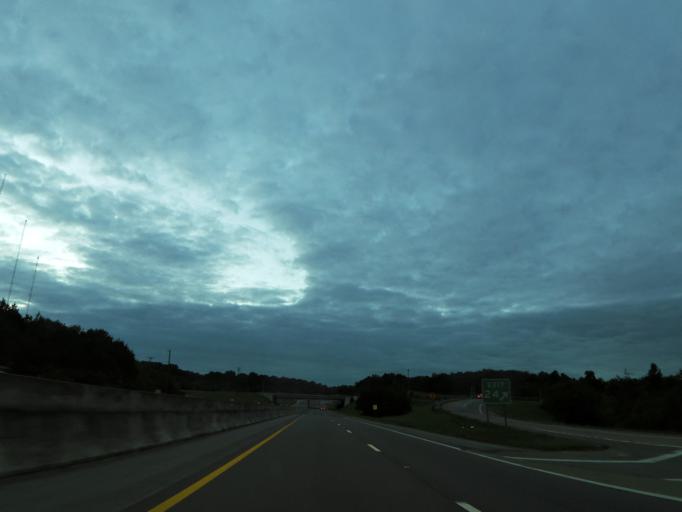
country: US
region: Tennessee
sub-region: Davidson County
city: Nashville
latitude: 36.2069
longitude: -86.8708
